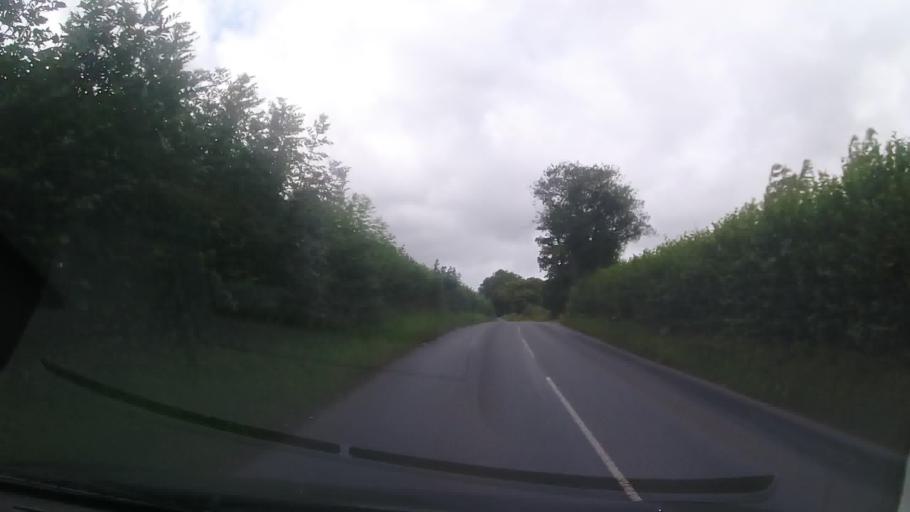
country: GB
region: England
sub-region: Shropshire
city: Craven Arms
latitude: 52.4386
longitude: -2.8562
